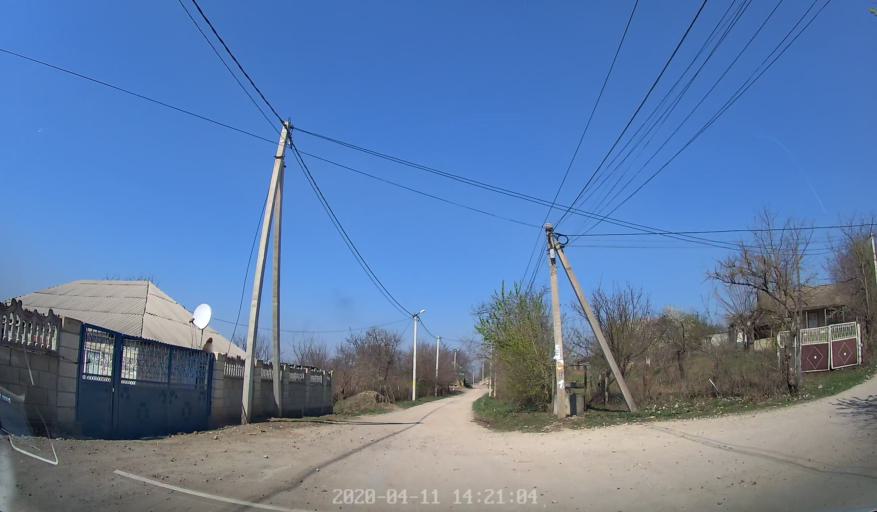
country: MD
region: Chisinau
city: Vadul lui Voda
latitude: 47.0871
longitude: 29.1349
